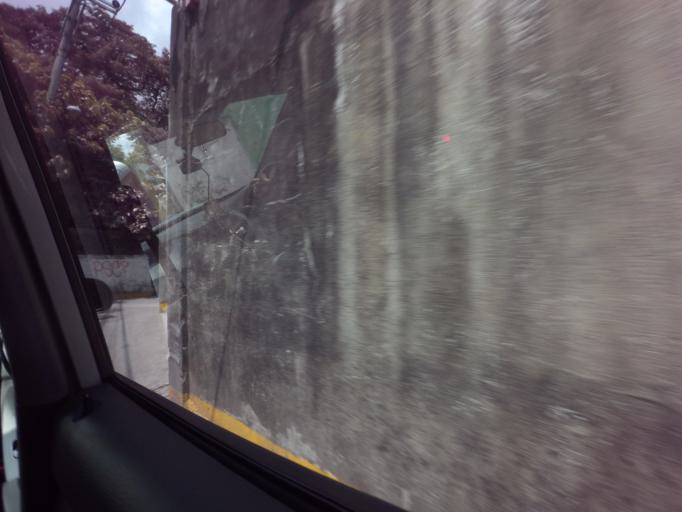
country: PH
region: Metro Manila
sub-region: San Juan
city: San Juan
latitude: 14.5928
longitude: 121.0131
